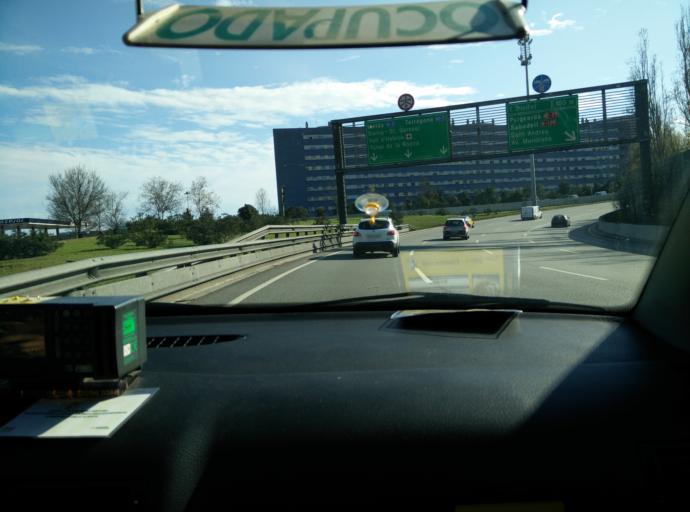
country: ES
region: Catalonia
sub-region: Provincia de Barcelona
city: Santa Coloma de Gramenet
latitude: 41.4496
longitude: 2.1936
